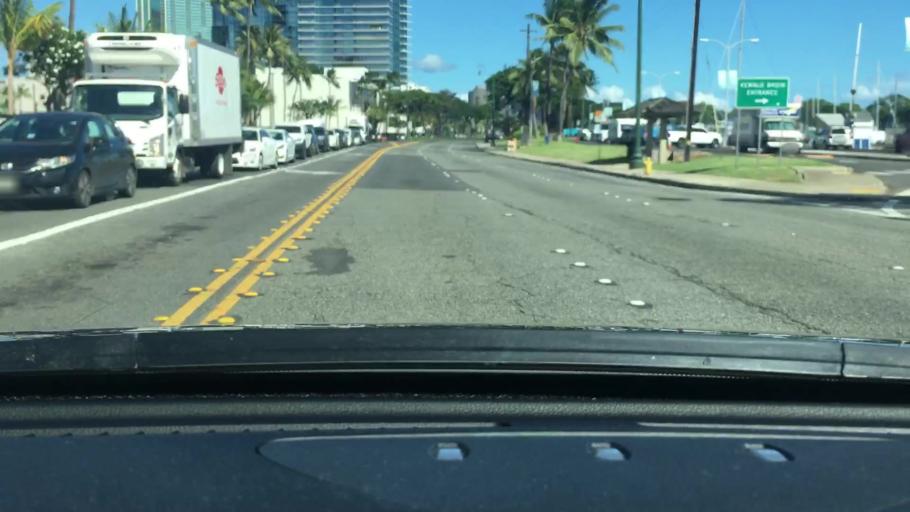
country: US
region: Hawaii
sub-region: Honolulu County
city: Honolulu
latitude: 21.2949
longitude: -157.8576
